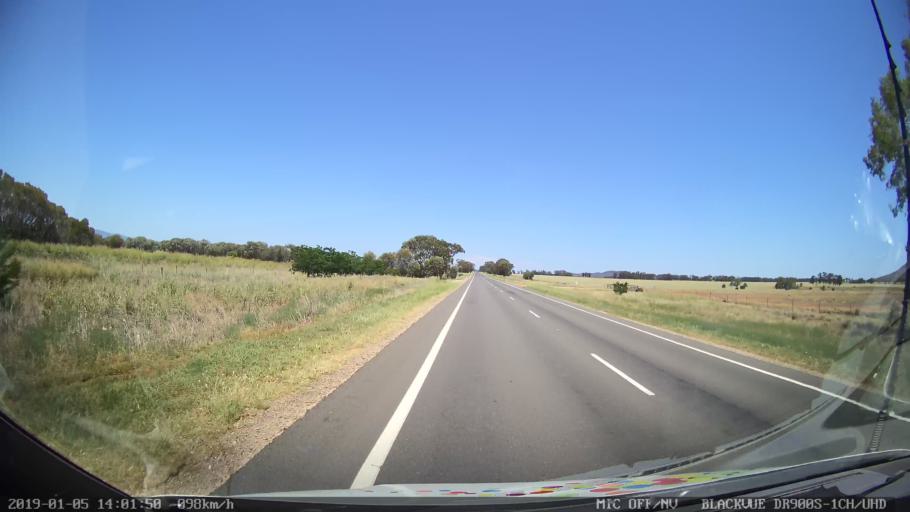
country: AU
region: New South Wales
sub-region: Gunnedah
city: Gunnedah
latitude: -31.1736
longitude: 150.3300
